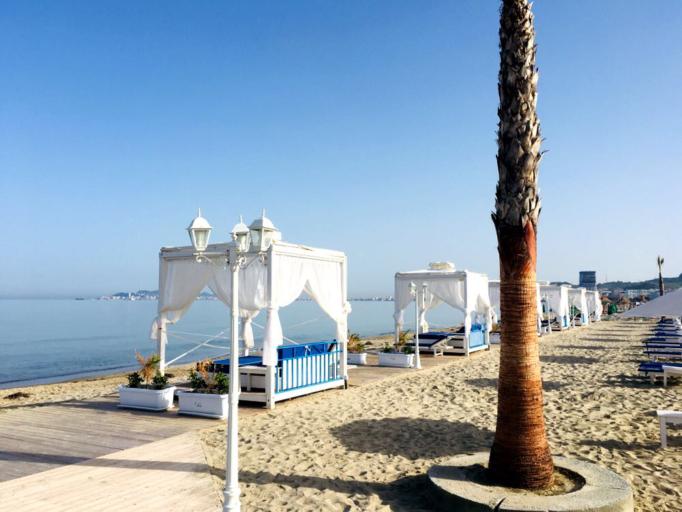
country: AL
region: Tirane
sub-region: Rrethi i Kavajes
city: Golem
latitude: 41.2462
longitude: 19.5195
